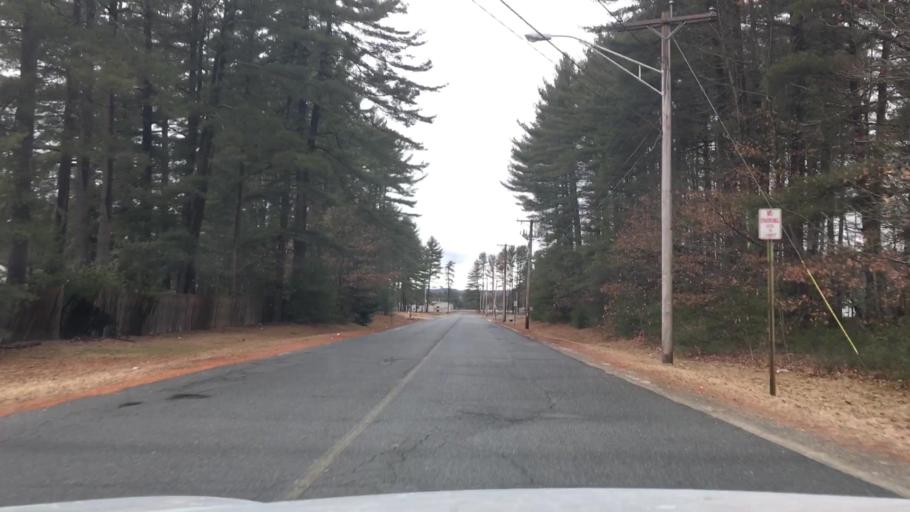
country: US
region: Massachusetts
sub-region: Franklin County
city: Orange
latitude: 42.5624
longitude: -72.2823
